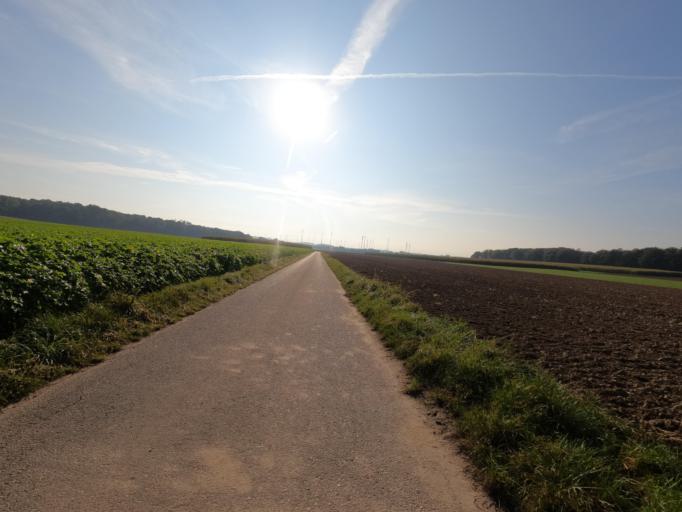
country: DE
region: North Rhine-Westphalia
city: Huckelhoven
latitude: 51.0438
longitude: 6.2664
